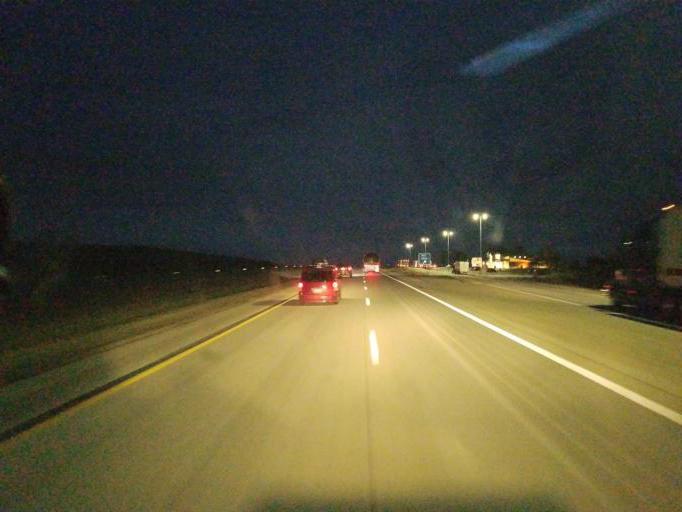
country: US
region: Iowa
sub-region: Guthrie County
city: Guthrie Center
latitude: 41.4967
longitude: -94.5648
